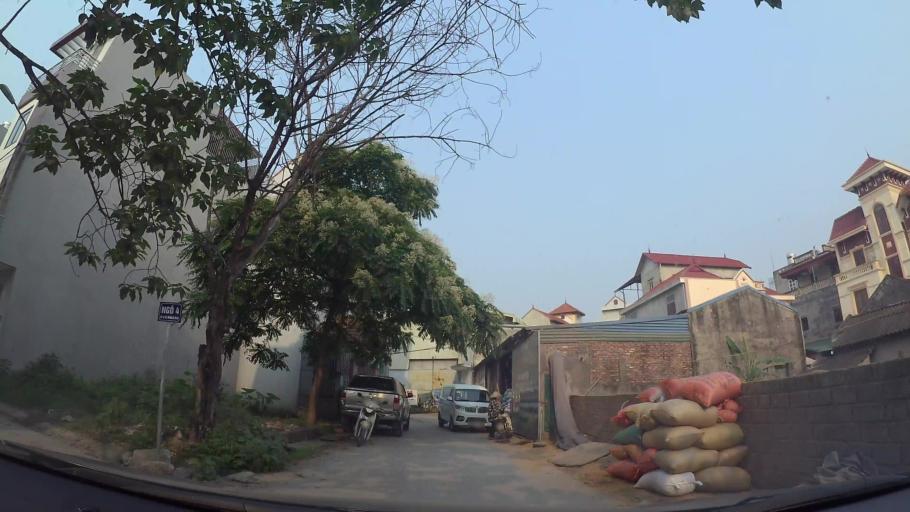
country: VN
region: Ha Noi
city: Thuong Tin
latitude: 20.8698
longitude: 105.8764
